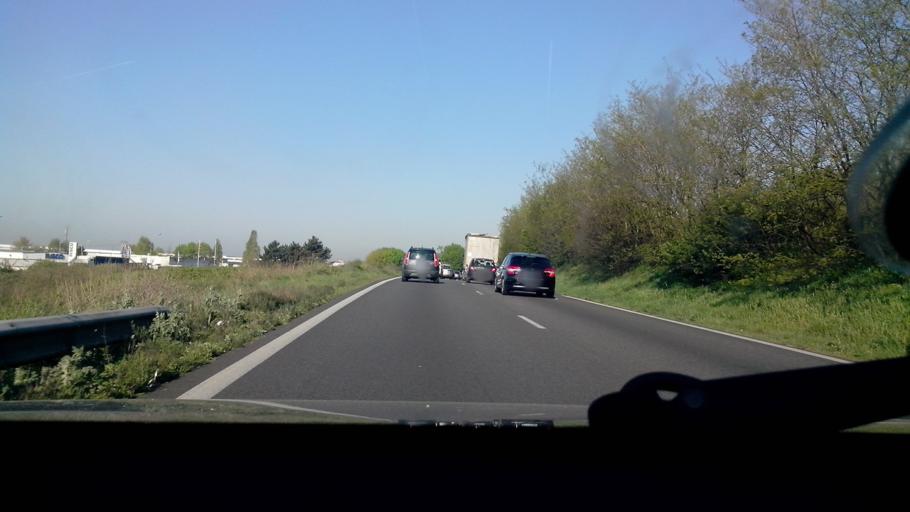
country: FR
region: Ile-de-France
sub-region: Departement de l'Essonne
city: Fleury-Merogis
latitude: 48.6249
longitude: 2.3686
